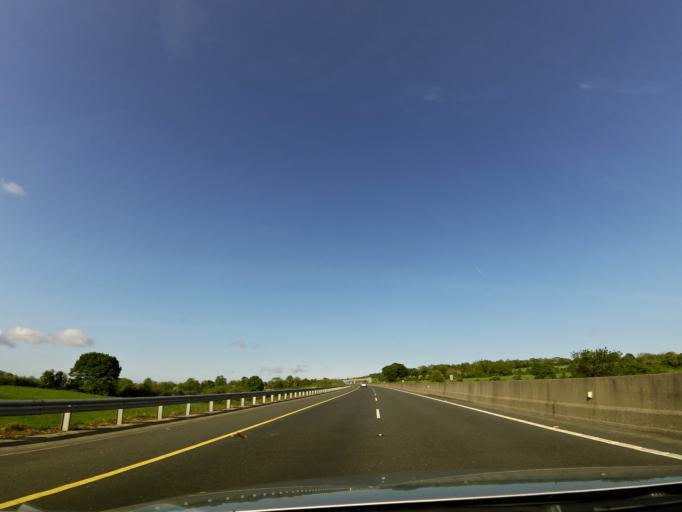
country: IE
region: Munster
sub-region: North Tipperary
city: Nenagh
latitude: 52.8445
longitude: -8.2618
